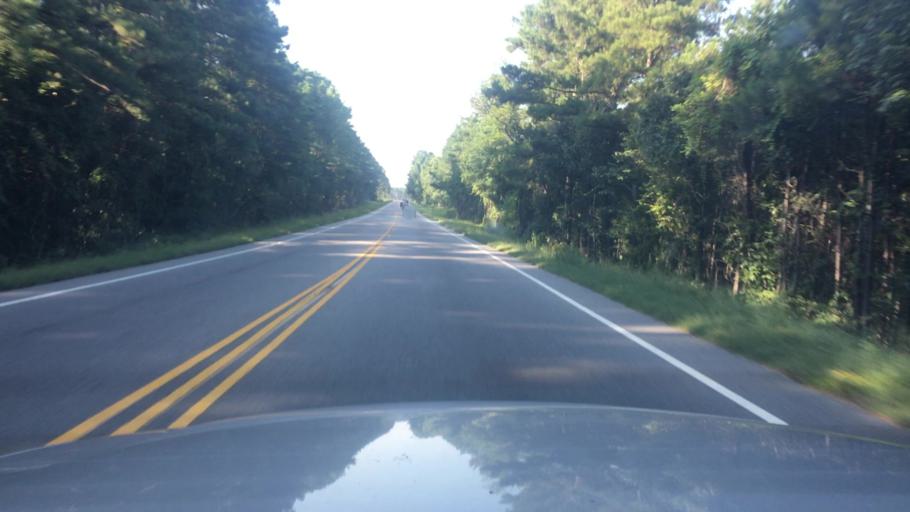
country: US
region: North Carolina
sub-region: Harnett County
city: Walkertown
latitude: 35.2035
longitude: -78.8493
